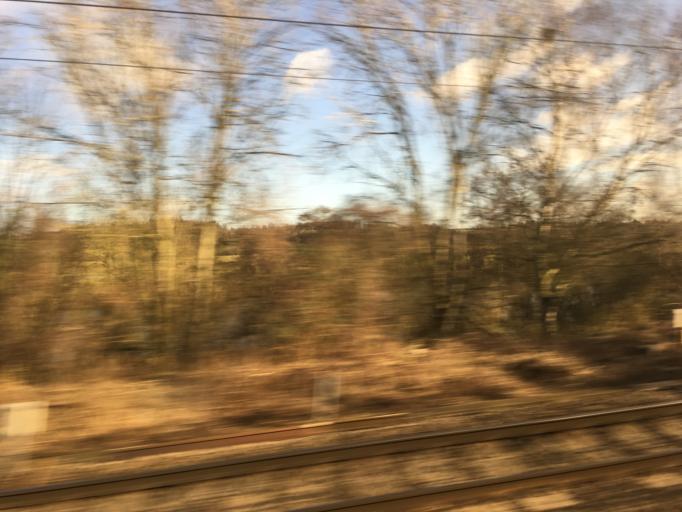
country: GB
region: England
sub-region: West Berkshire
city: Tilehurst
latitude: 51.4695
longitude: -1.0255
